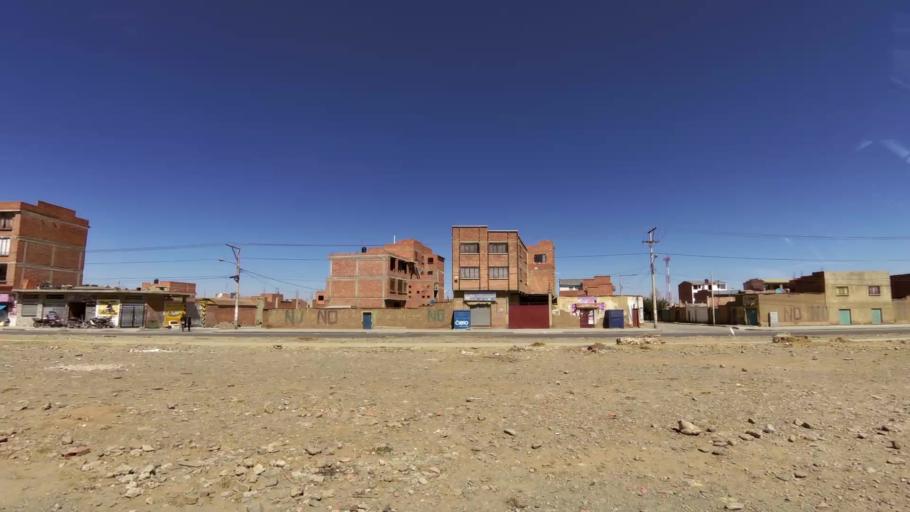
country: BO
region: La Paz
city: La Paz
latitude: -16.5322
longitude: -68.2098
